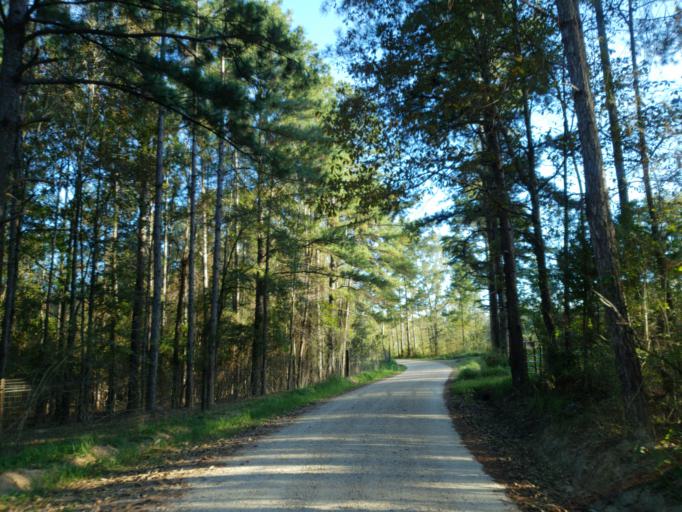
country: US
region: Mississippi
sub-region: Perry County
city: Richton
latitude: 31.3515
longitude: -88.8057
